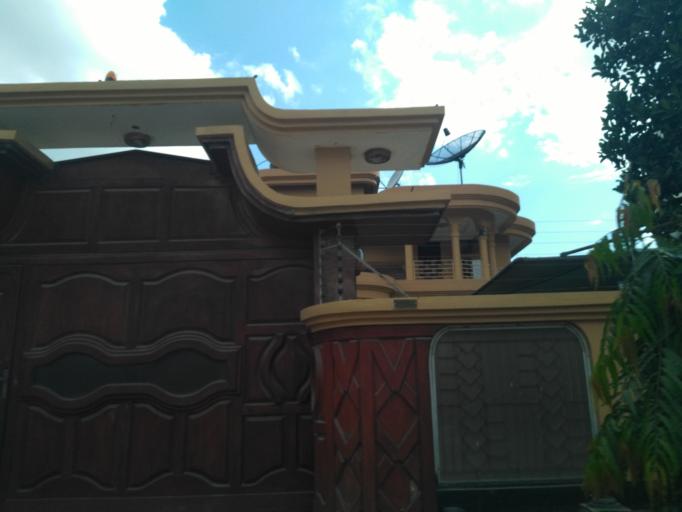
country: TZ
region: Dar es Salaam
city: Magomeni
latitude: -6.7633
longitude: 39.2461
